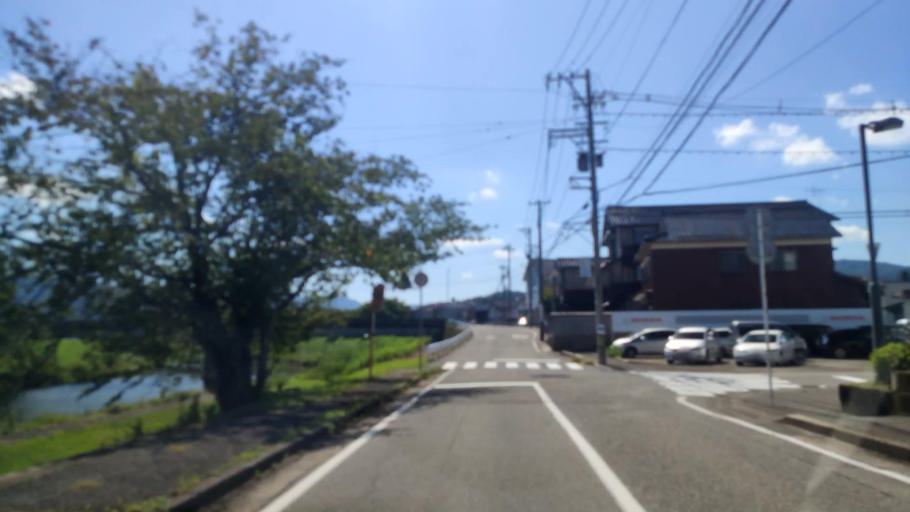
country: JP
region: Ishikawa
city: Nanao
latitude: 37.3904
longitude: 136.8999
